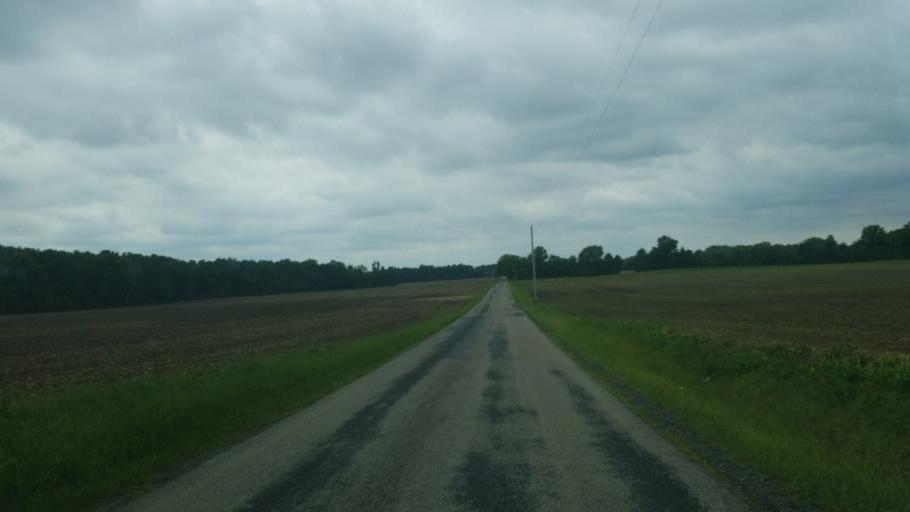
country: US
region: Ohio
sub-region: Fairfield County
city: Baltimore
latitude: 39.8669
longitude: -82.5860
